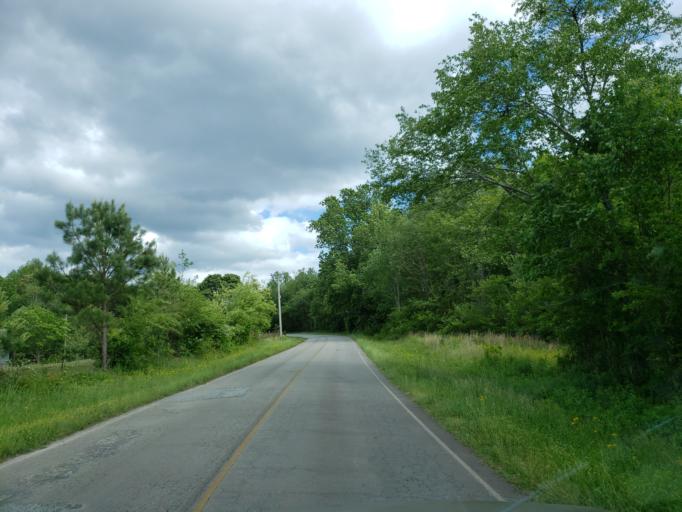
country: US
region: Georgia
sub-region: Haralson County
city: Tallapoosa
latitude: 33.6840
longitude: -85.3153
